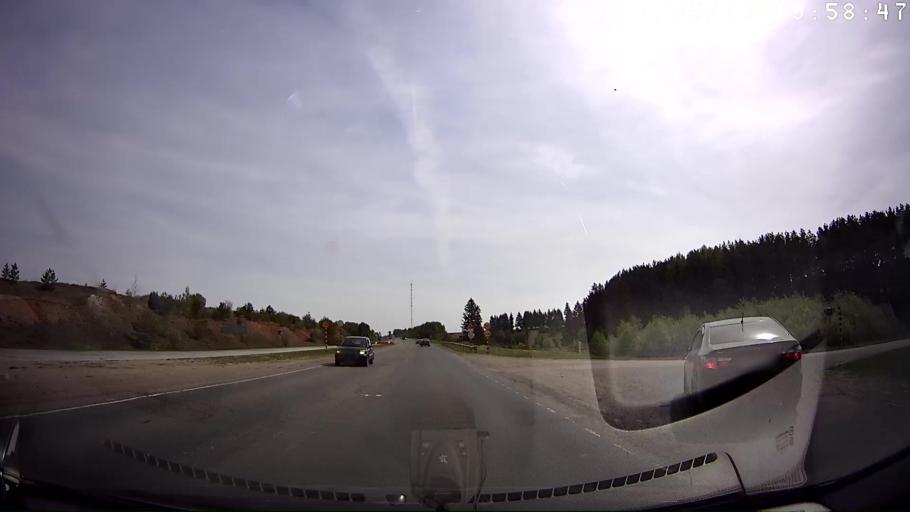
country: RU
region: Mariy-El
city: Sovetskiy
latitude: 56.7527
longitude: 48.5012
